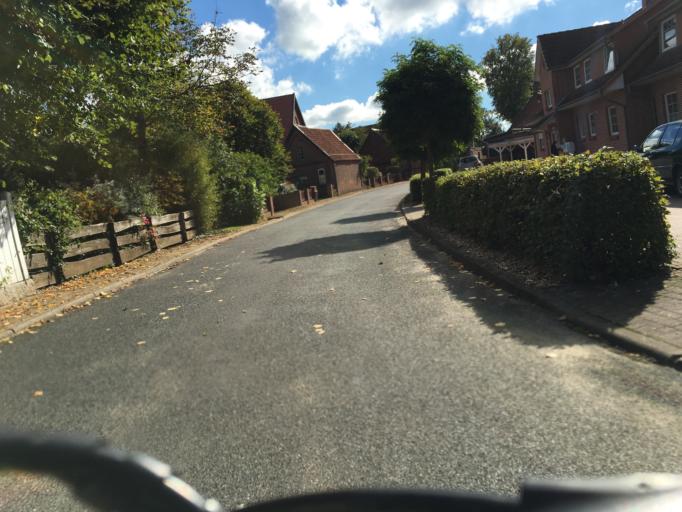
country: DE
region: Lower Saxony
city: Bardowick
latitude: 53.2982
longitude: 10.3967
